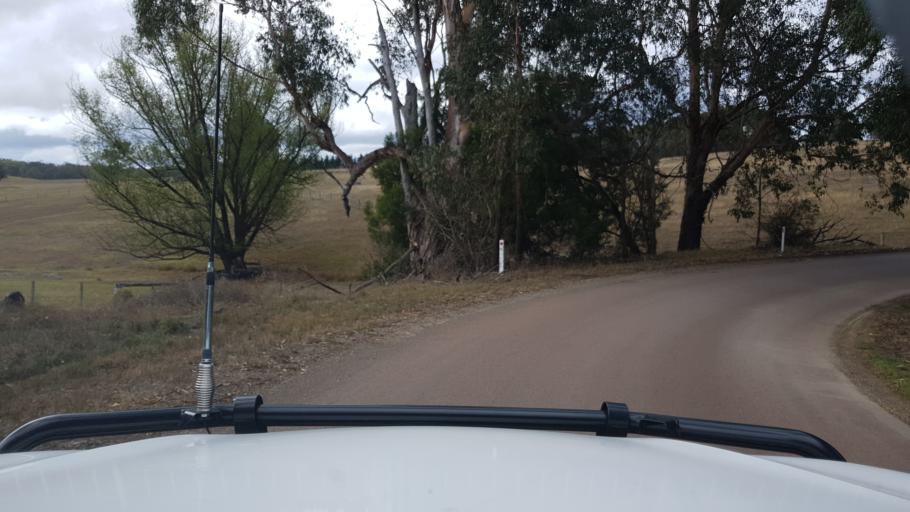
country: AU
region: Victoria
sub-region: East Gippsland
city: Bairnsdale
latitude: -37.7856
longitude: 147.5875
